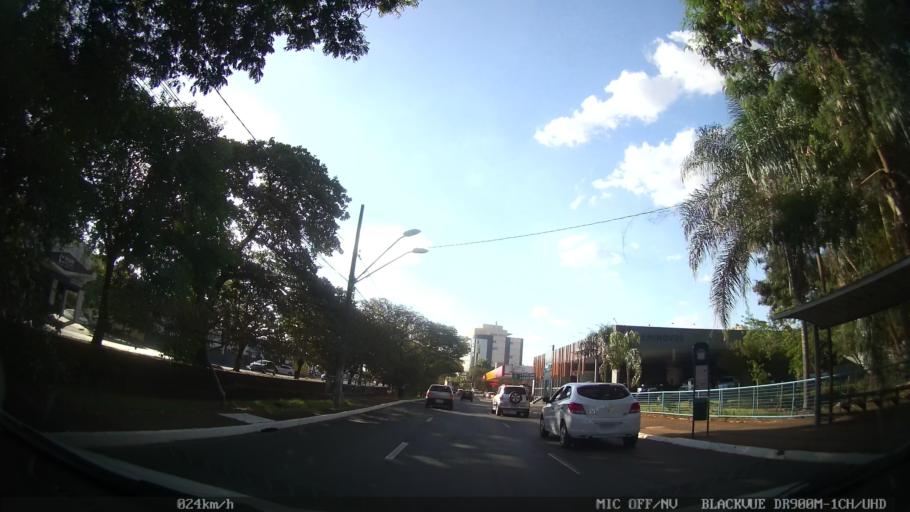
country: BR
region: Sao Paulo
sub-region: Ribeirao Preto
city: Ribeirao Preto
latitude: -21.1899
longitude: -47.7976
